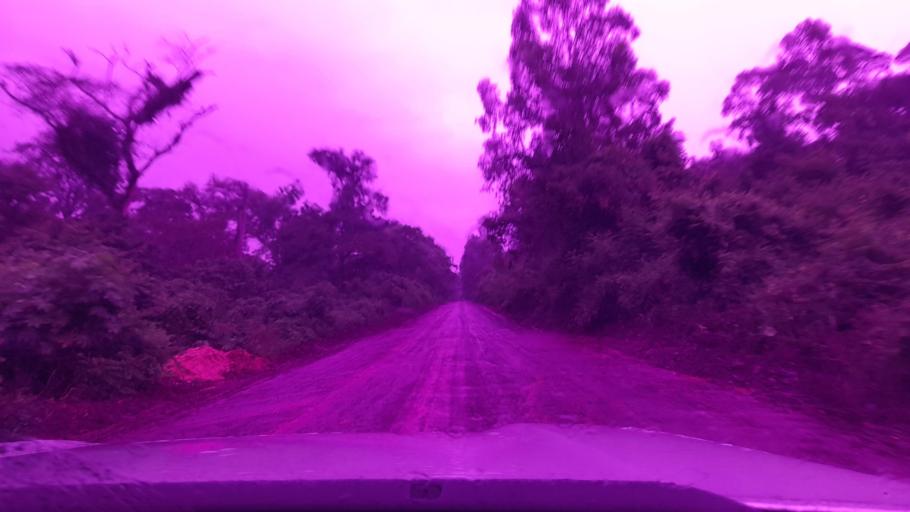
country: ET
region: Oromiya
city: Metu
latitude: 8.3246
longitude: 35.6017
